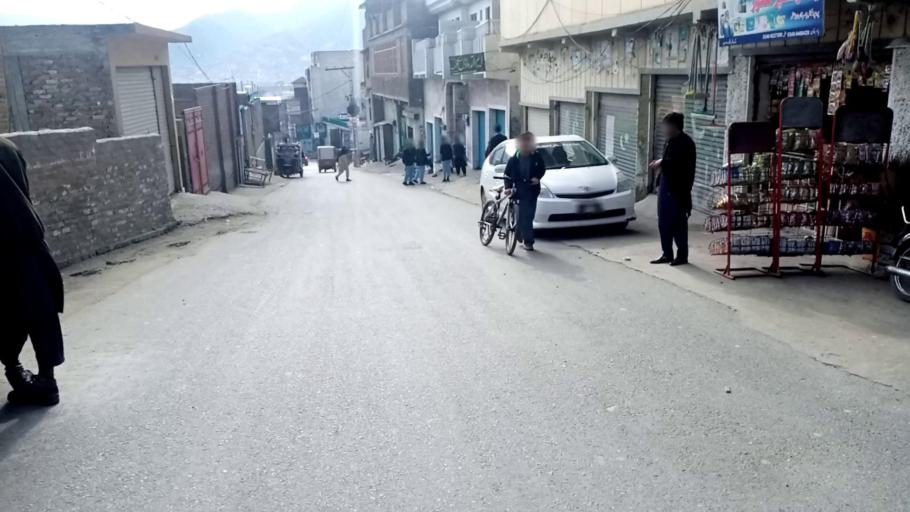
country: PK
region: Khyber Pakhtunkhwa
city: Mingora
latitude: 34.7737
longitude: 72.3678
